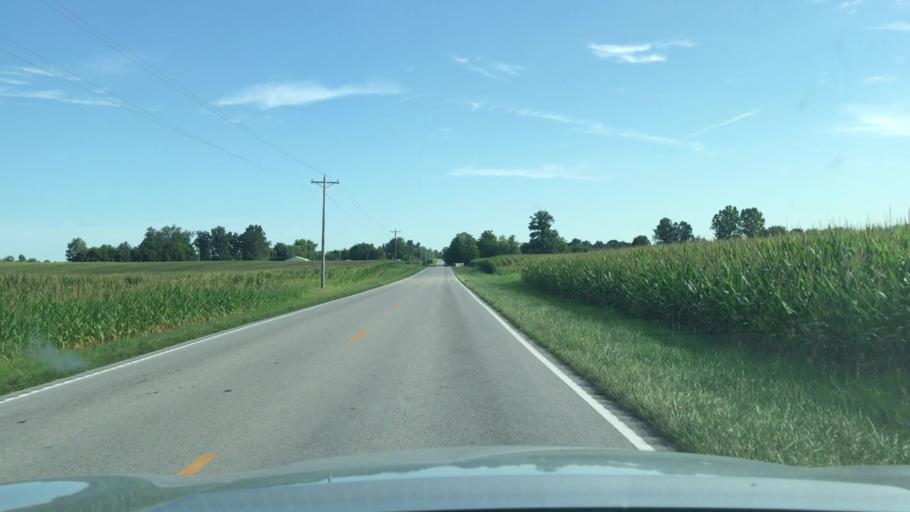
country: US
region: Kentucky
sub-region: Todd County
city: Elkton
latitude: 36.9202
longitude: -87.1628
